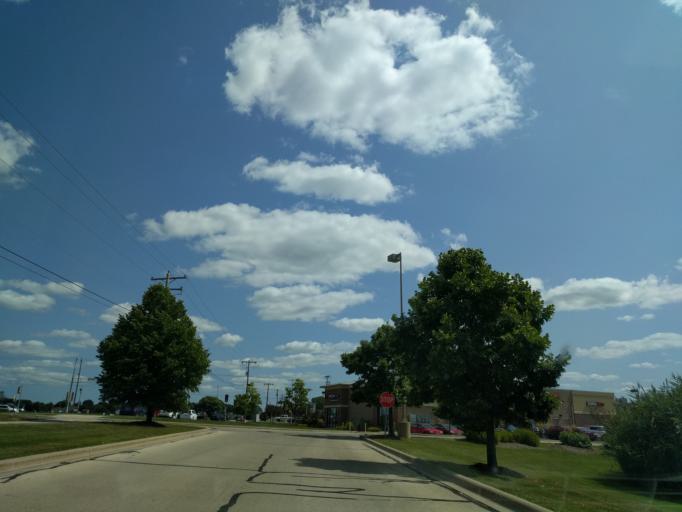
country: US
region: Wisconsin
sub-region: Brown County
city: Allouez
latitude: 44.4658
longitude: -87.9842
